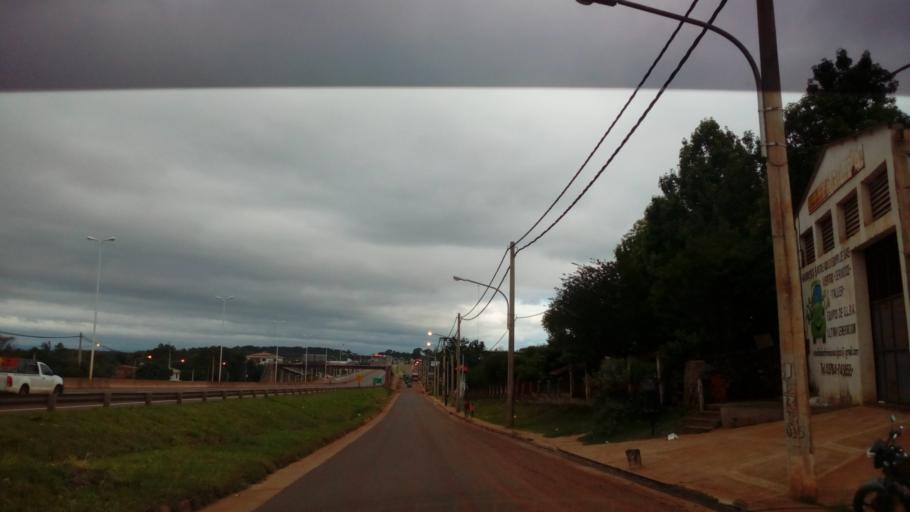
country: AR
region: Misiones
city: Garupa
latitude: -27.4564
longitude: -55.8568
